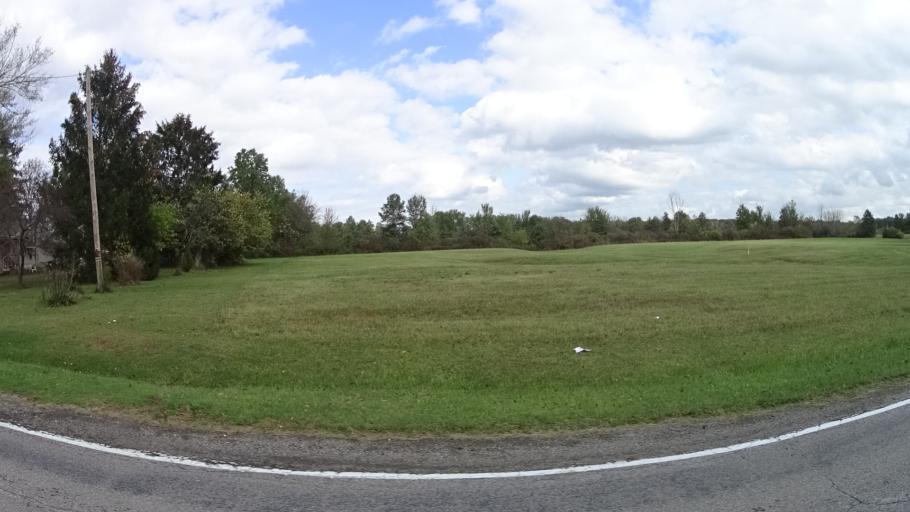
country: US
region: Ohio
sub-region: Lorain County
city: Eaton Estates
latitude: 41.3238
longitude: -82.0410
